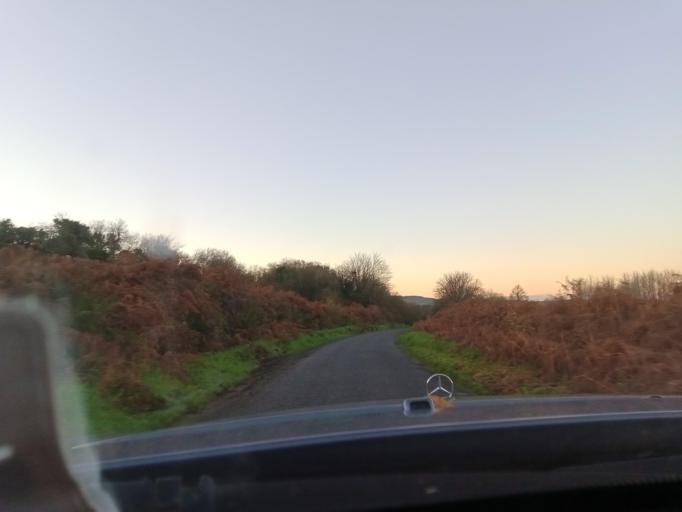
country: IE
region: Leinster
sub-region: Kilkenny
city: Thomastown
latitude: 52.4327
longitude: -7.1045
